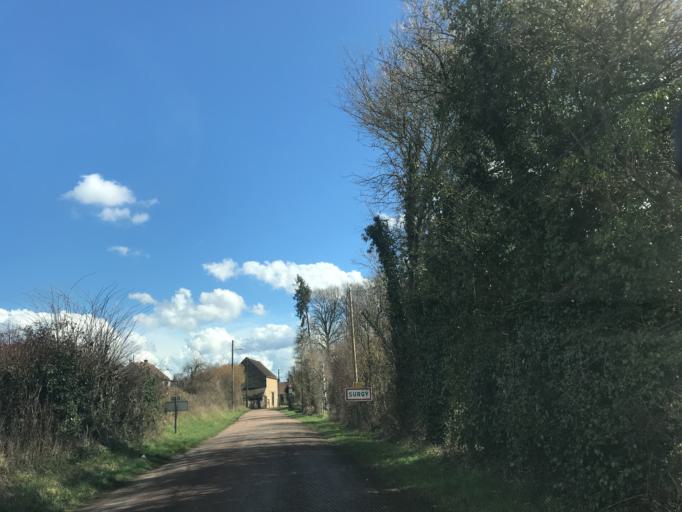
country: FR
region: Bourgogne
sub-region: Departement de la Nievre
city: Clamecy
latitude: 47.5100
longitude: 3.5096
